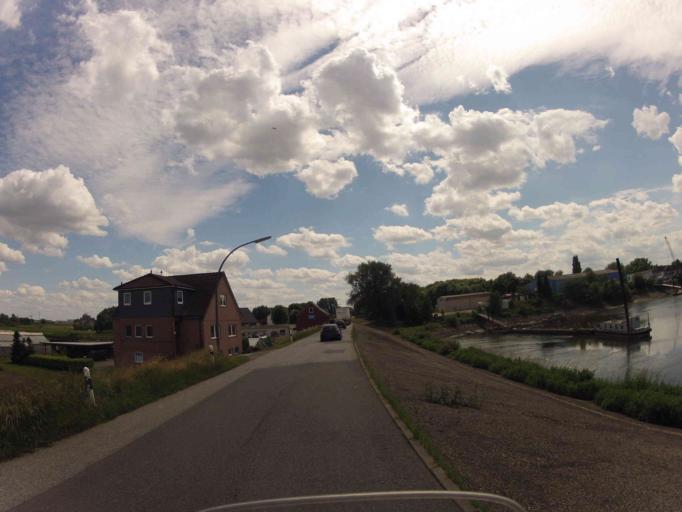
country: DE
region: Hamburg
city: Rothenburgsort
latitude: 53.5123
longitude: 10.0746
